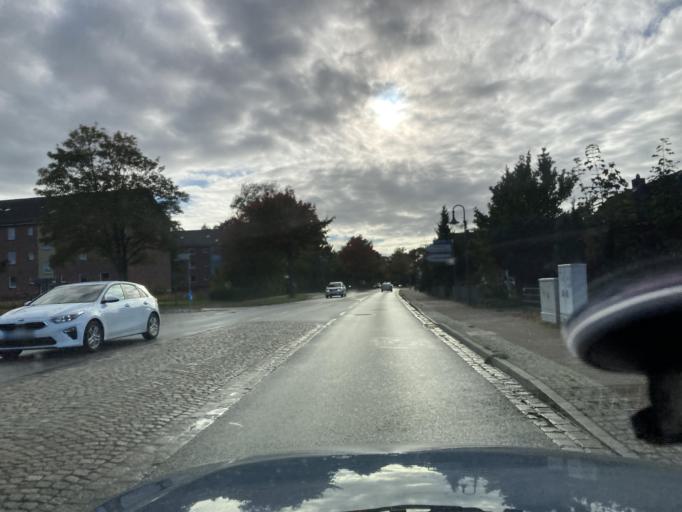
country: DE
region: Schleswig-Holstein
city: Budelsdorf
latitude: 54.3196
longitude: 9.6894
